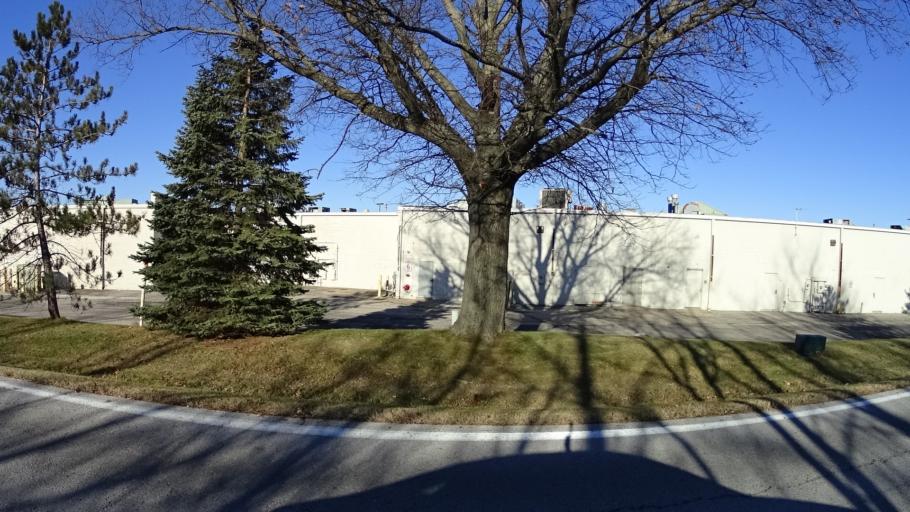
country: US
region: Ohio
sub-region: Lorain County
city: Sheffield
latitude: 41.3967
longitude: -82.1043
